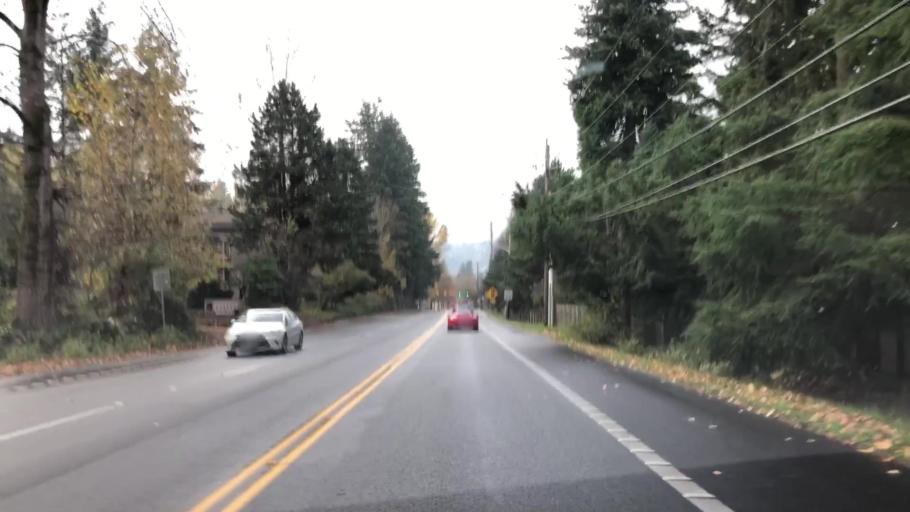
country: US
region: Washington
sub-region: King County
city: Woodinville
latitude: 47.7583
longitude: -122.1479
